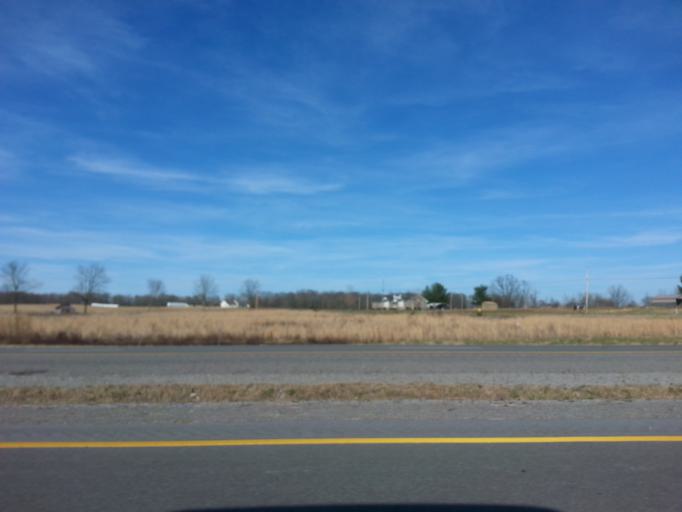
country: US
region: Tennessee
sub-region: Warren County
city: McMinnville
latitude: 35.7118
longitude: -85.8394
